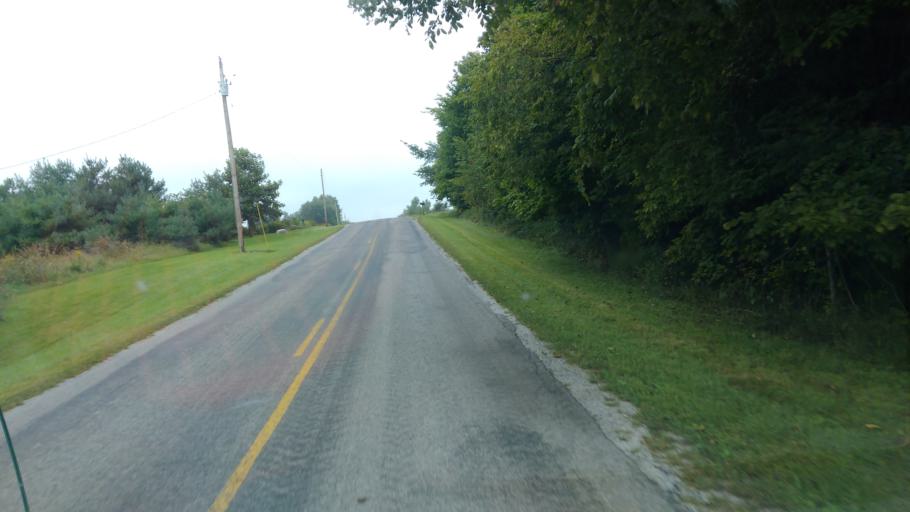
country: US
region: Ohio
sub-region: Hardin County
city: Kenton
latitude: 40.5687
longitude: -83.6351
